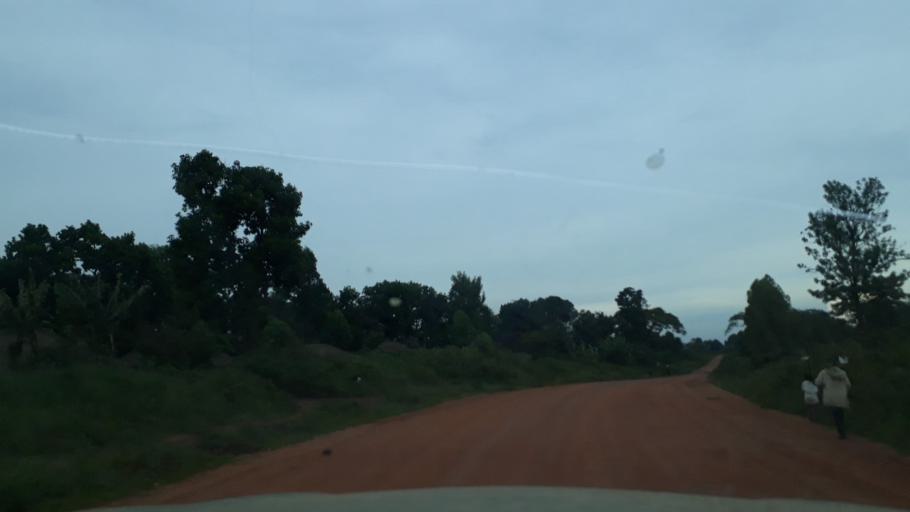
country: UG
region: Northern Region
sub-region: Zombo District
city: Paidha
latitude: 2.1697
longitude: 30.6953
